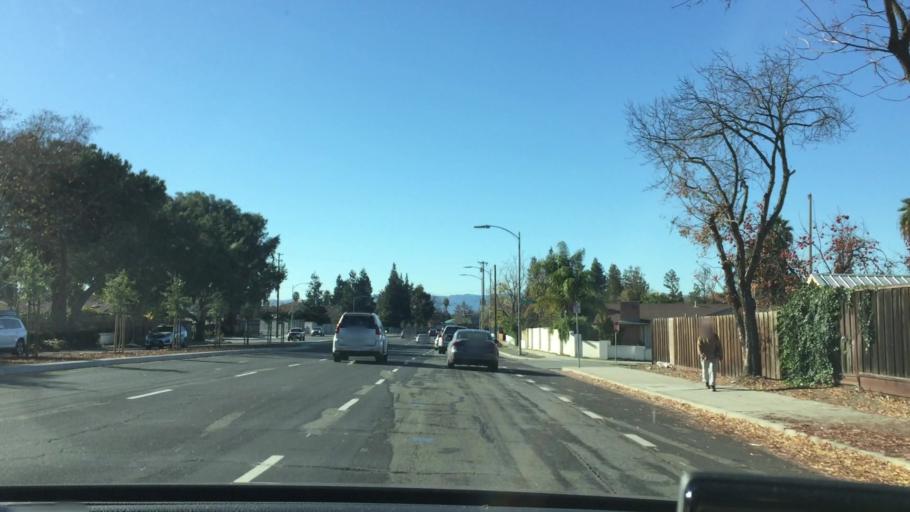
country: US
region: California
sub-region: Santa Clara County
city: Milpitas
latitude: 37.3900
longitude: -121.8803
